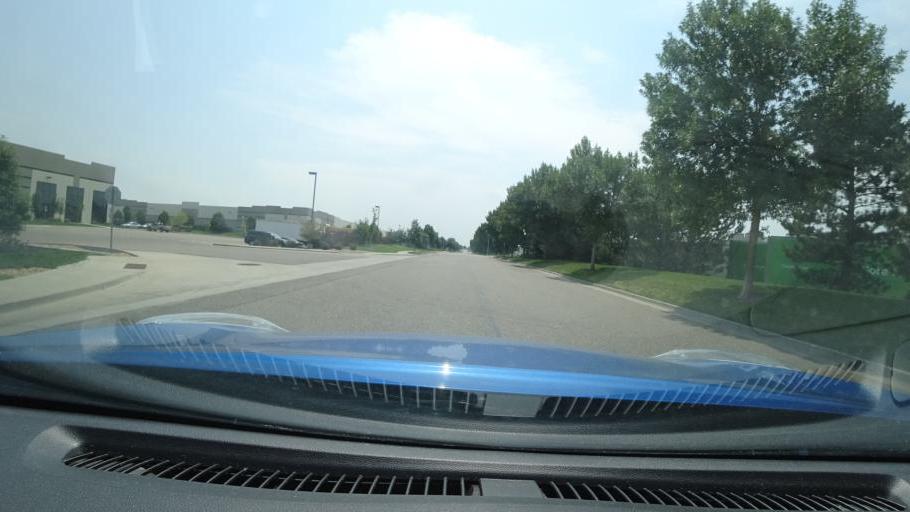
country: US
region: Colorado
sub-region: Adams County
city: Aurora
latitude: 39.7669
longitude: -104.7609
